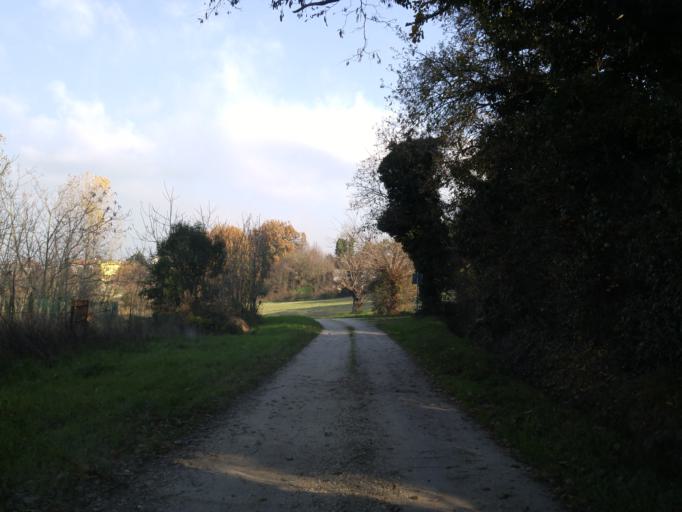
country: IT
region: The Marches
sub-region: Provincia di Pesaro e Urbino
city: Villanova
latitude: 43.7397
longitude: 12.9248
